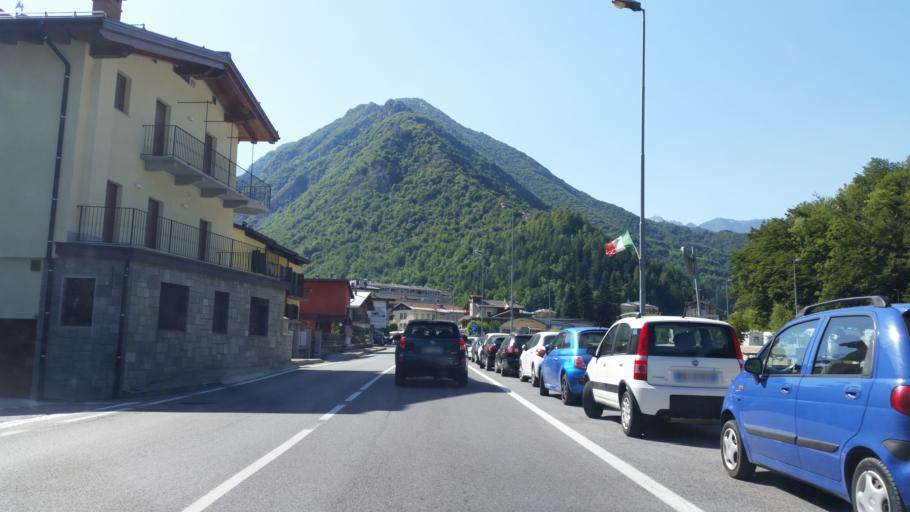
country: IT
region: Piedmont
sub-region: Provincia di Cuneo
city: Vernante
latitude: 44.2457
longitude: 7.5324
